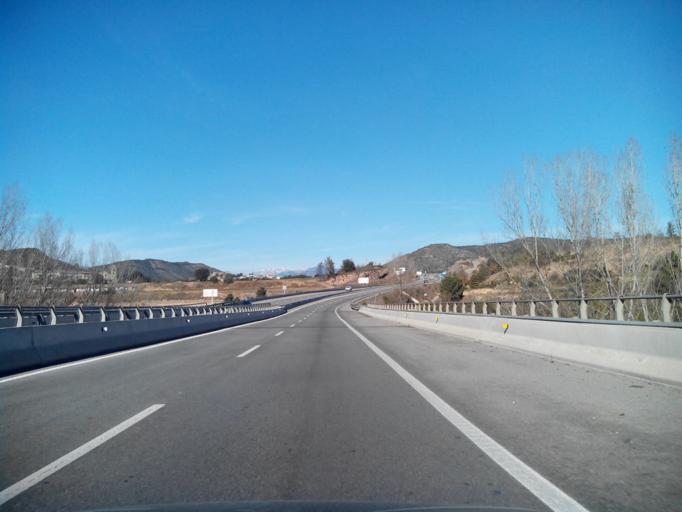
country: ES
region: Catalonia
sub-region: Provincia de Barcelona
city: Puig-reig
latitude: 41.9516
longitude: 1.8838
